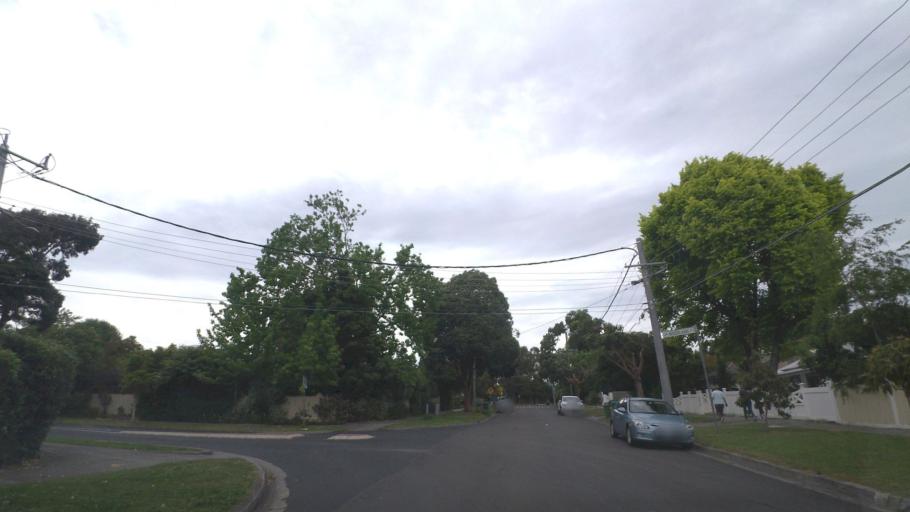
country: AU
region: Victoria
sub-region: Maroondah
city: Croydon Hills
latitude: -37.7943
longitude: 145.2667
